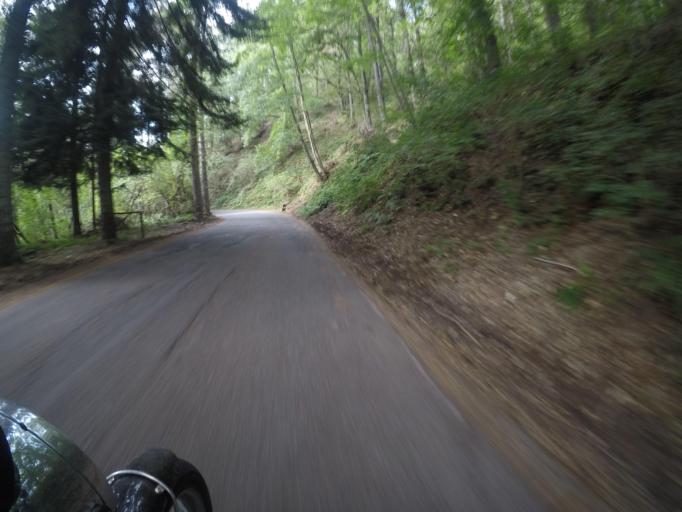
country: IT
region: Tuscany
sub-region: Provincia di Massa-Carrara
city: Fosdinovo
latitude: 44.1204
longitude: 10.0697
